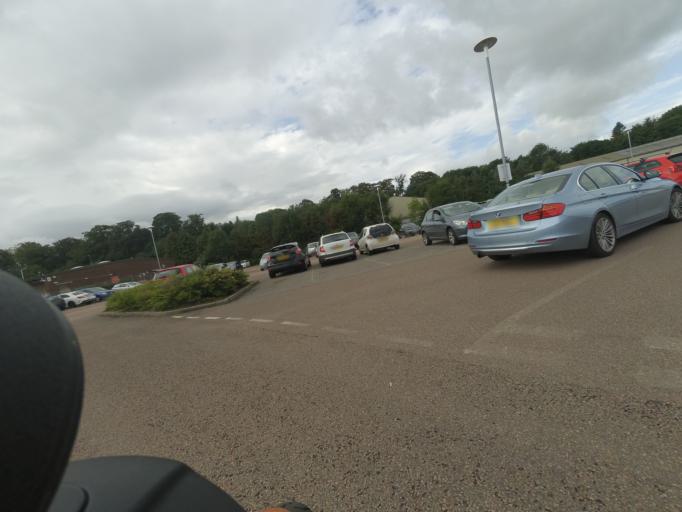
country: GB
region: Scotland
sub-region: Perth and Kinross
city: Blairgowrie
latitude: 56.5891
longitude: -3.3344
